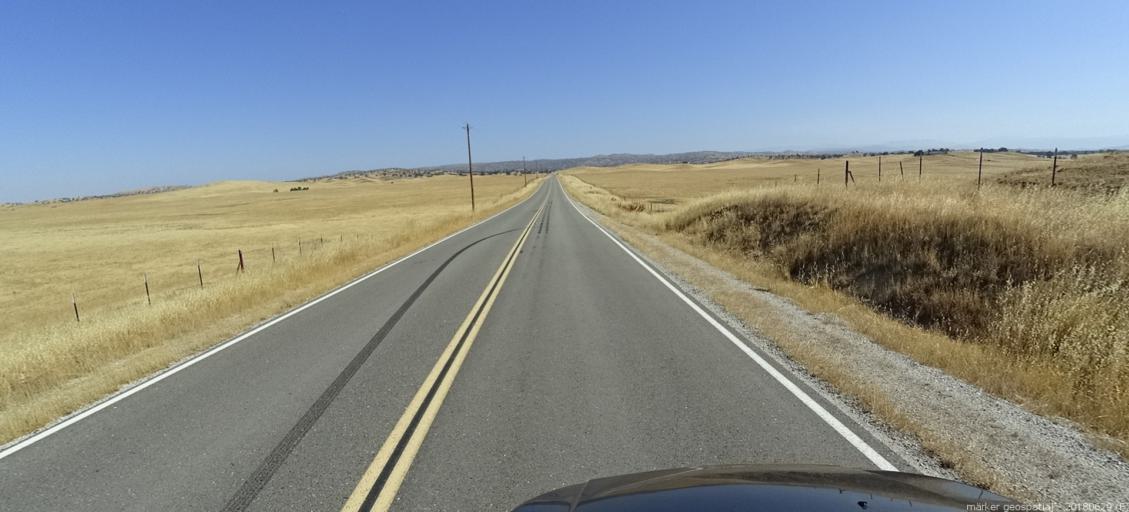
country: US
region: California
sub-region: Madera County
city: Bonadelle Ranchos-Madera Ranchos
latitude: 37.0313
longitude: -119.7938
